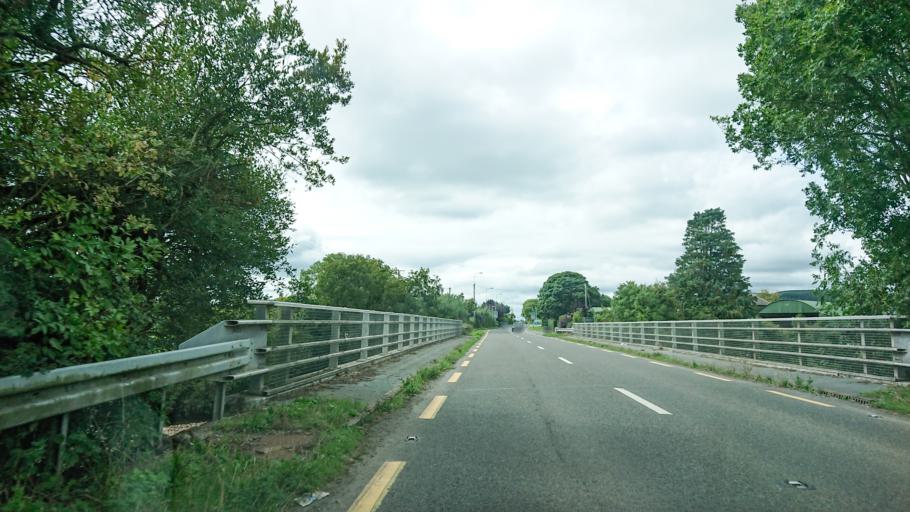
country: IE
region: Munster
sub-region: Waterford
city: Dungarvan
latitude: 52.1080
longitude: -7.6612
